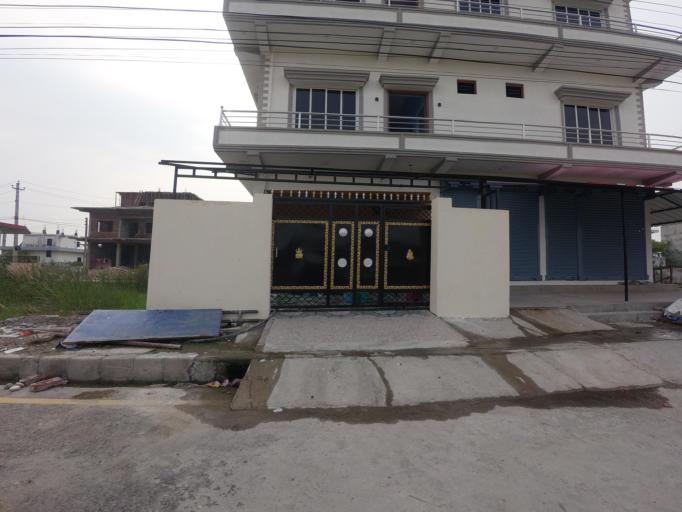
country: NP
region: Western Region
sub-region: Lumbini Zone
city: Bhairahawa
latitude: 27.4954
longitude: 83.4517
